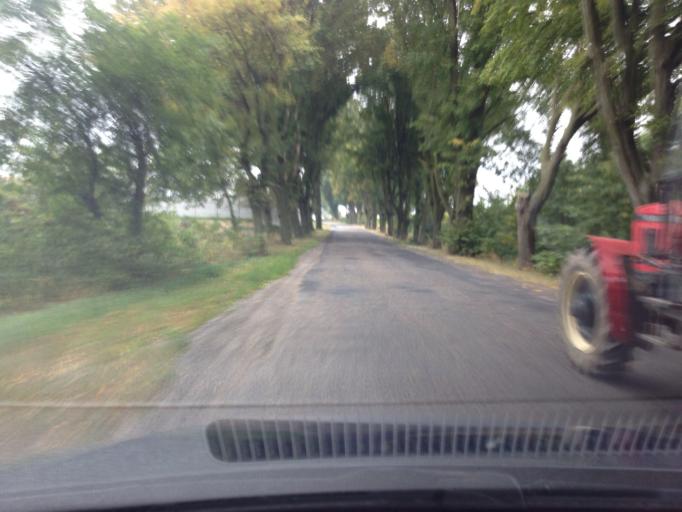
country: PL
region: Kujawsko-Pomorskie
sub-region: Powiat brodnicki
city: Gorzno
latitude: 53.2103
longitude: 19.6358
